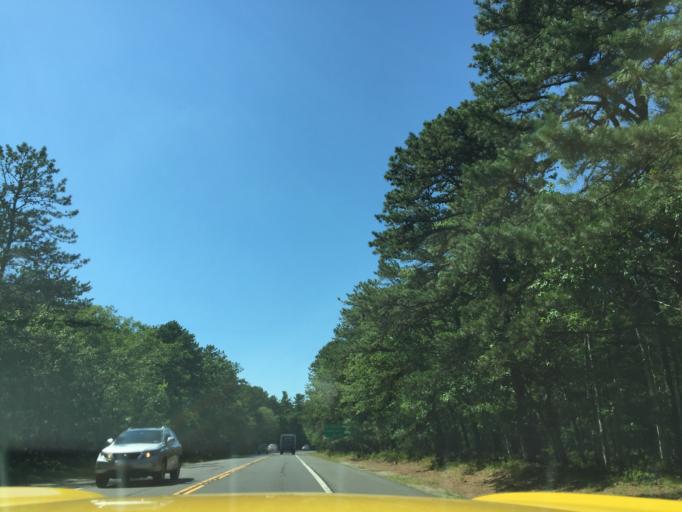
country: US
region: New York
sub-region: Suffolk County
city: Sag Harbor
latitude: 40.9857
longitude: -72.2593
